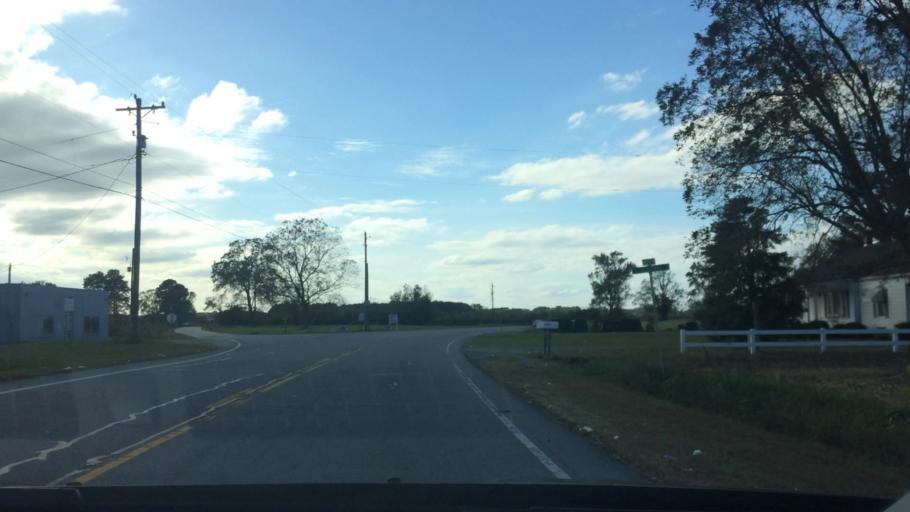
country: US
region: North Carolina
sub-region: Greene County
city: Snow Hill
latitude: 35.4367
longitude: -77.7693
